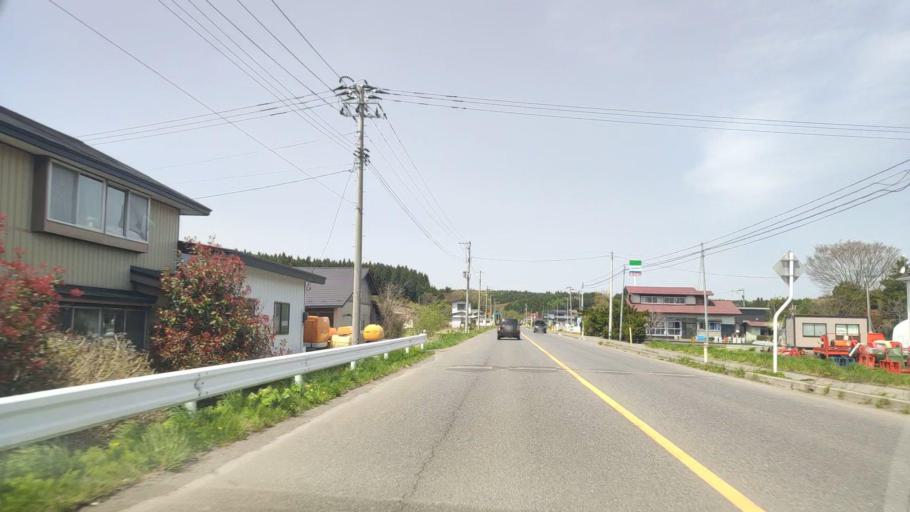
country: JP
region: Aomori
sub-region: Misawa Shi
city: Inuotose
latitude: 40.5584
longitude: 141.3869
